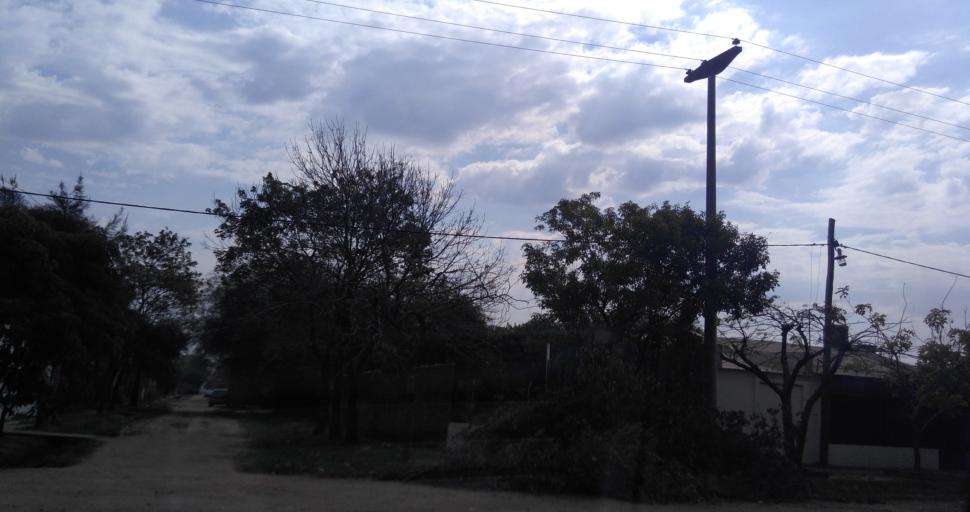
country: AR
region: Chaco
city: Fontana
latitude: -27.4517
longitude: -59.0368
